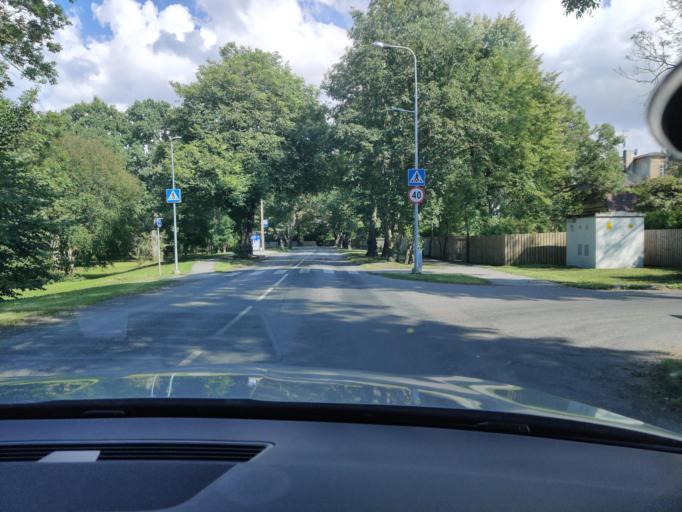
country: EE
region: Harju
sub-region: Viimsi vald
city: Viimsi
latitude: 59.4578
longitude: 24.8241
